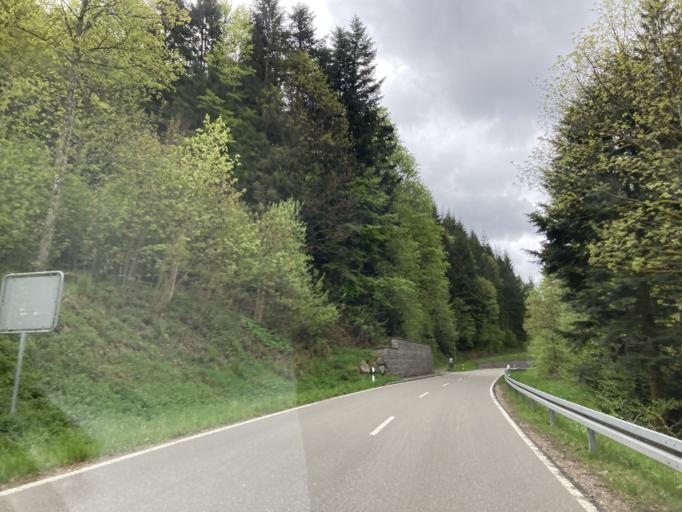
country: DE
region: Baden-Wuerttemberg
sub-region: Freiburg Region
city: Schonach im Schwarzwald
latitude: 48.1714
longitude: 8.1594
